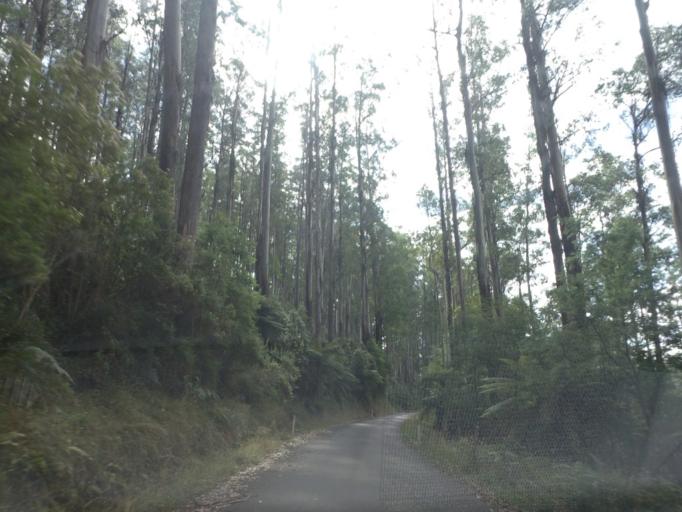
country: AU
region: Victoria
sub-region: Yarra Ranges
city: Millgrove
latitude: -37.5950
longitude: 145.7001
